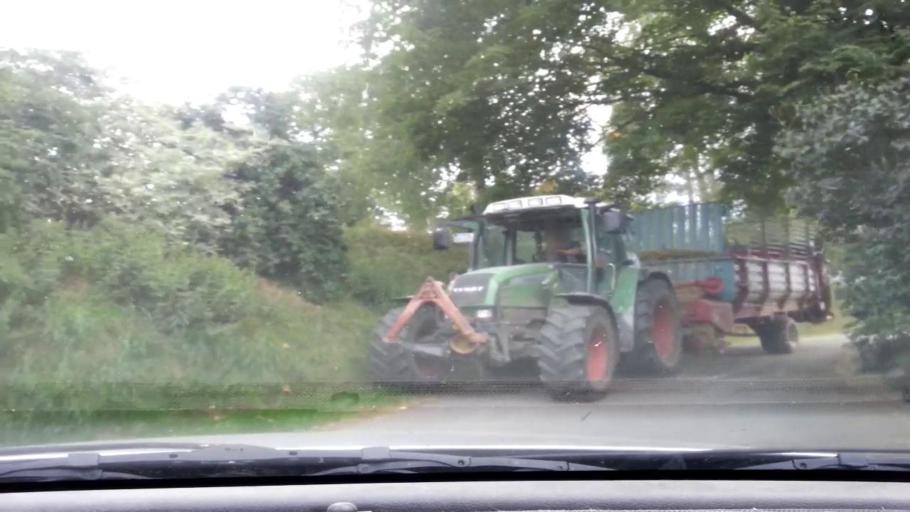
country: DE
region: Bavaria
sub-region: Upper Palatinate
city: Krummennaab
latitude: 49.8312
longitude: 12.0755
